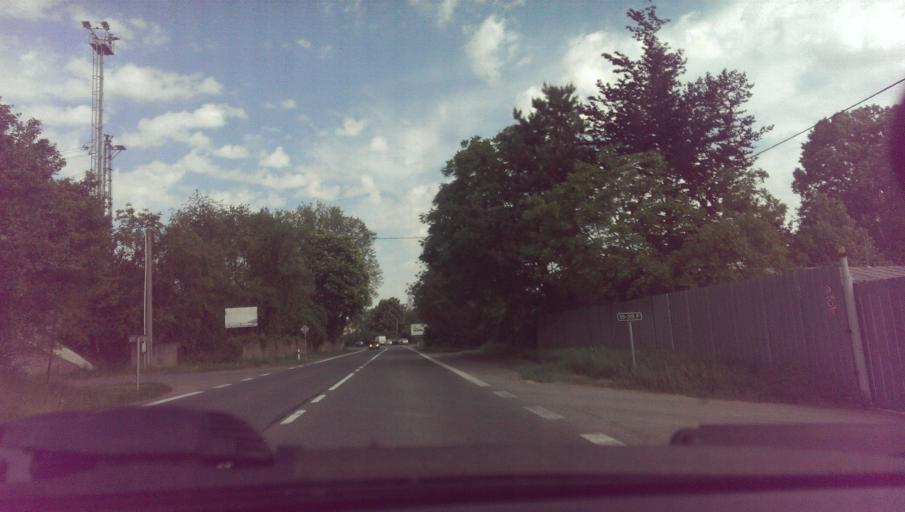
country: CZ
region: Zlin
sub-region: Okres Zlin
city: Napajedla
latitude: 49.1618
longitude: 17.5052
